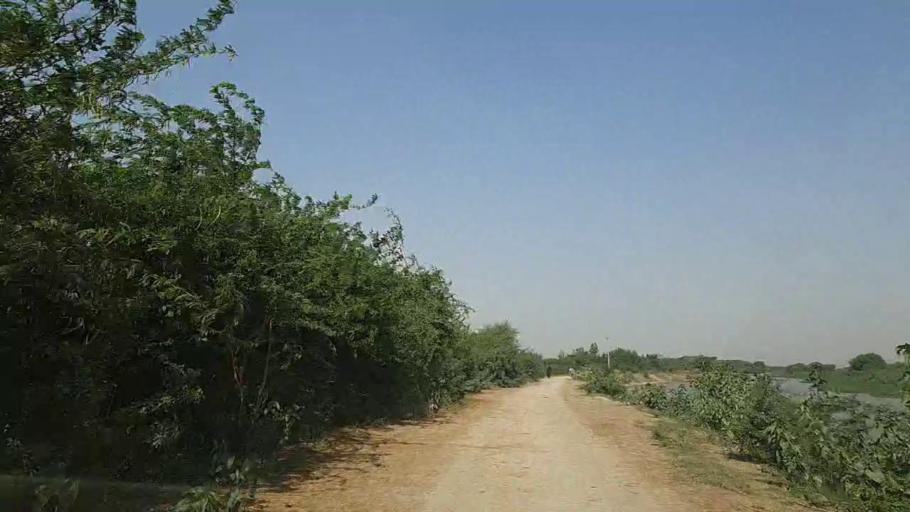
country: PK
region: Sindh
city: Daro Mehar
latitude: 24.7271
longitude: 68.1556
